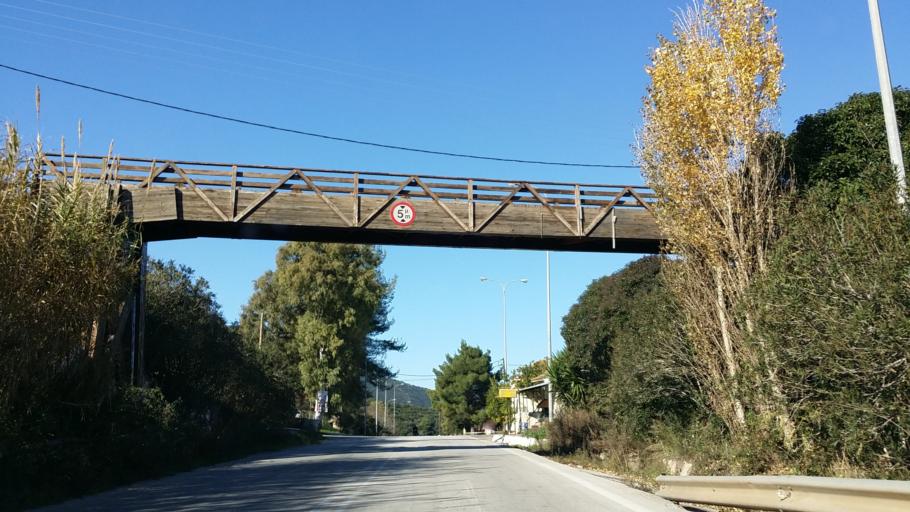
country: GR
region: West Greece
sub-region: Nomos Aitolias kai Akarnanias
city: Monastirakion
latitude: 38.9091
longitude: 20.9521
